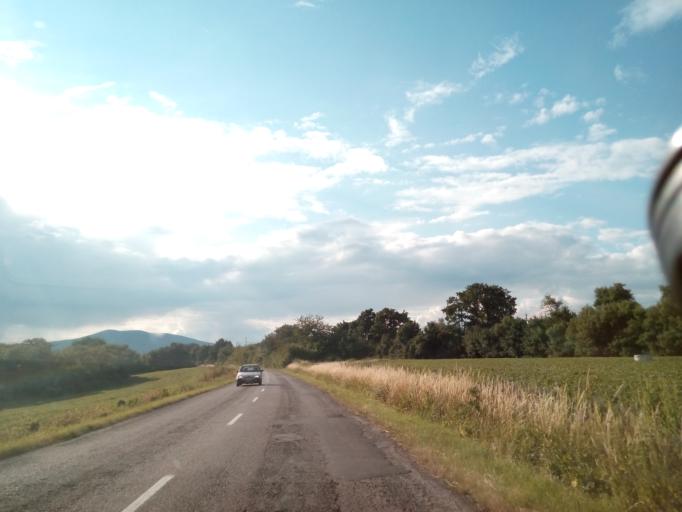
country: SK
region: Kosicky
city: Secovce
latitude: 48.6096
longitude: 21.5508
